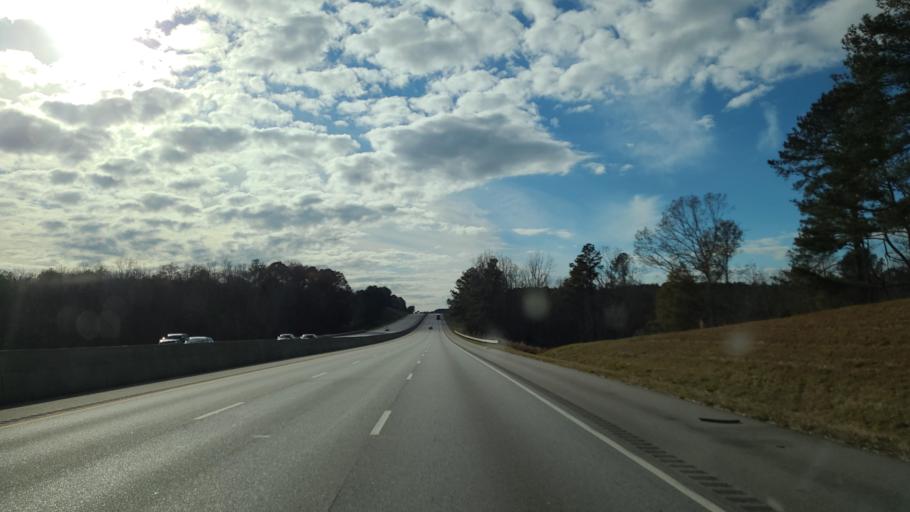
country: US
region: Georgia
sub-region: Haralson County
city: Tallapoosa
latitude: 33.6601
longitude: -85.3939
